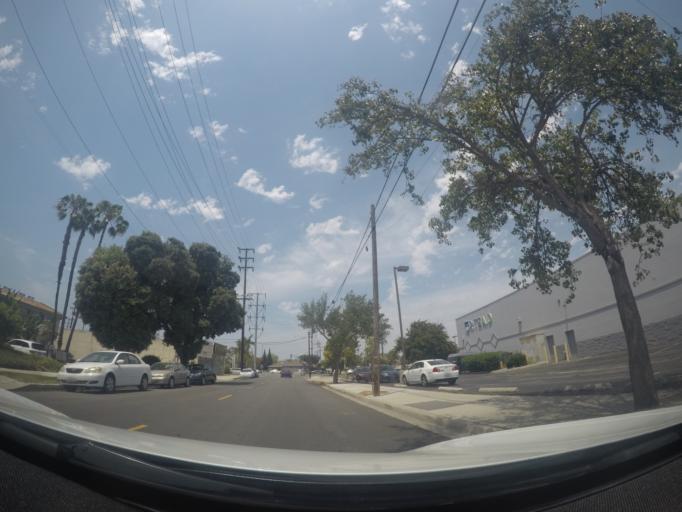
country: US
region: California
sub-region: Los Angeles County
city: Torrance
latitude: 33.8248
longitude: -118.3544
